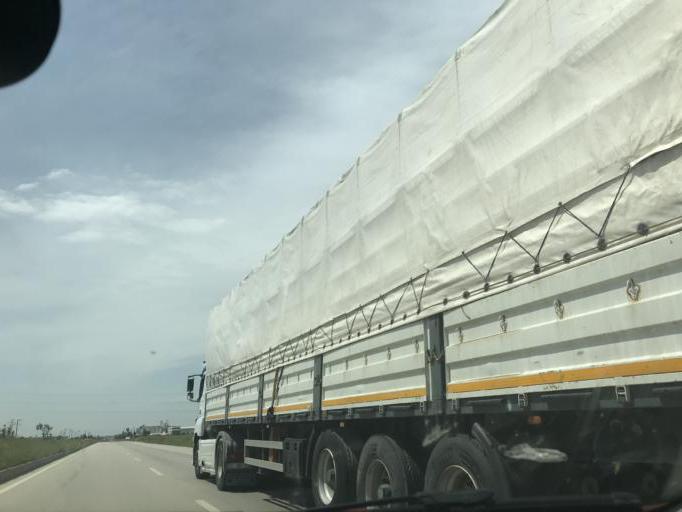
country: TR
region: Adana
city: Yuregir
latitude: 36.9792
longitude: 35.4590
